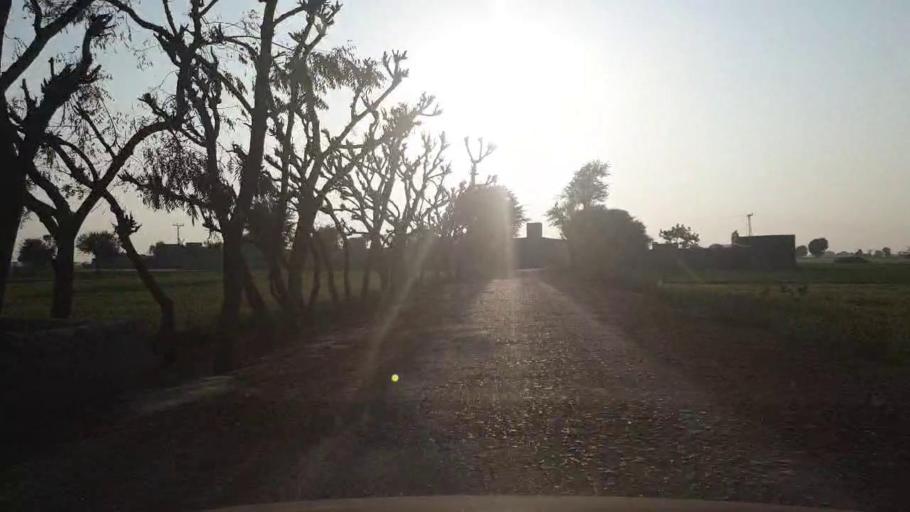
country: PK
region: Sindh
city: Hala
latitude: 25.8605
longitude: 68.4070
